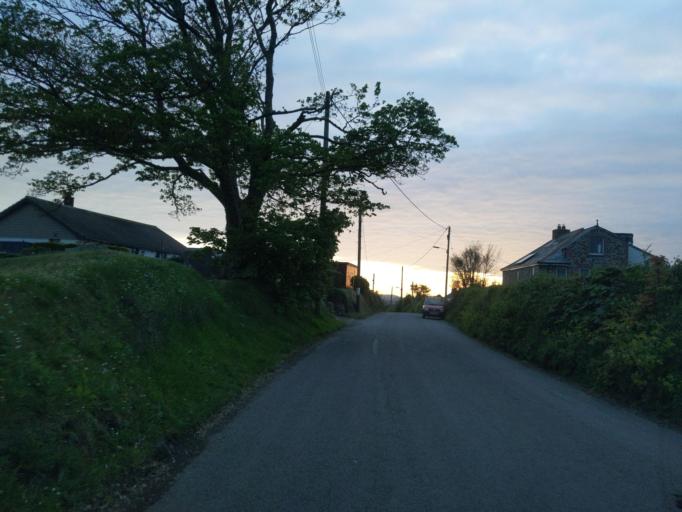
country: GB
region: England
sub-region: Cornwall
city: Polzeath
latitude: 50.5589
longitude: -4.8753
